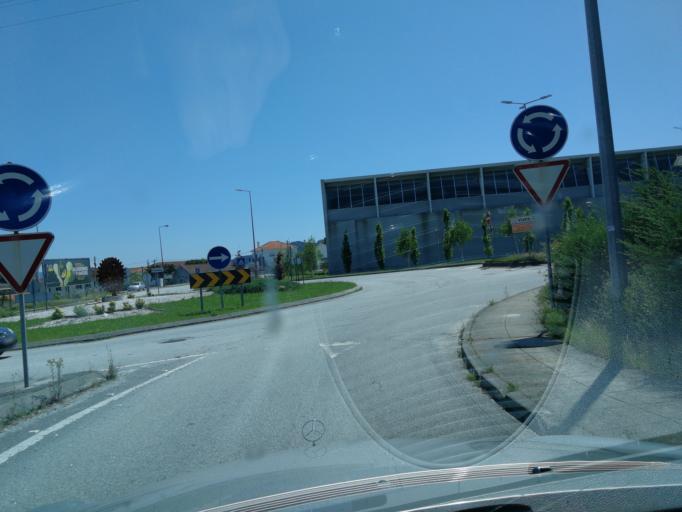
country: PT
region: Viana do Castelo
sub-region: Viana do Castelo
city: Meadela
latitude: 41.7105
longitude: -8.8030
